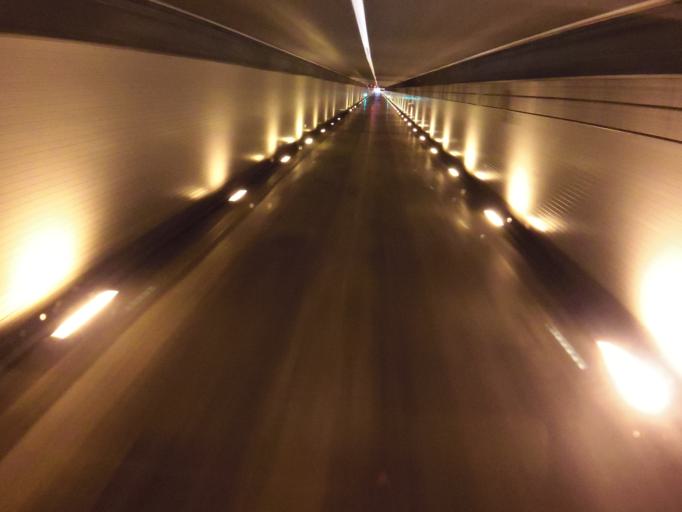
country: US
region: West Virginia
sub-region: Mercer County
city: Princeton
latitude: 37.2754
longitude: -81.1239
